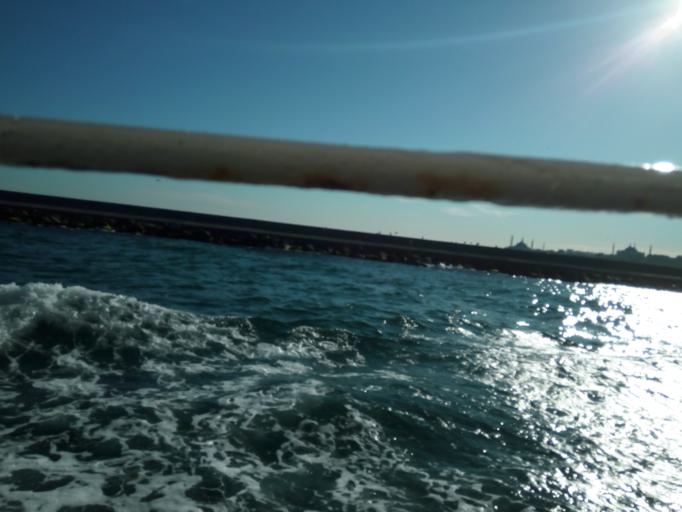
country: TR
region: Istanbul
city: UEskuedar
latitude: 41.0067
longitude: 29.0043
